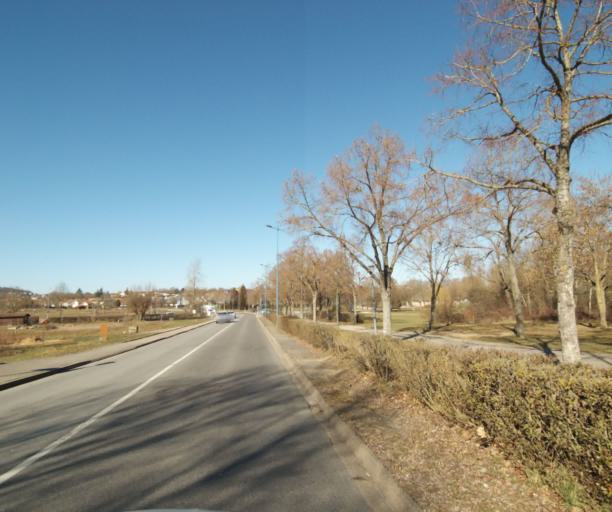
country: FR
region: Lorraine
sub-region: Departement de Meurthe-et-Moselle
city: Vandoeuvre-les-Nancy
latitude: 48.6468
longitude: 6.1972
